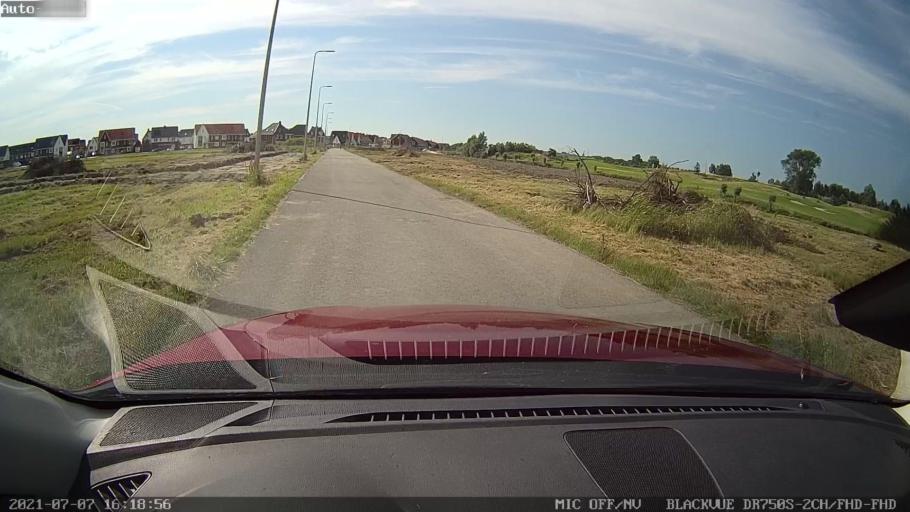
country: NL
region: Zeeland
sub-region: Gemeente Middelburg
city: Middelburg
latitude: 51.4861
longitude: 3.6430
